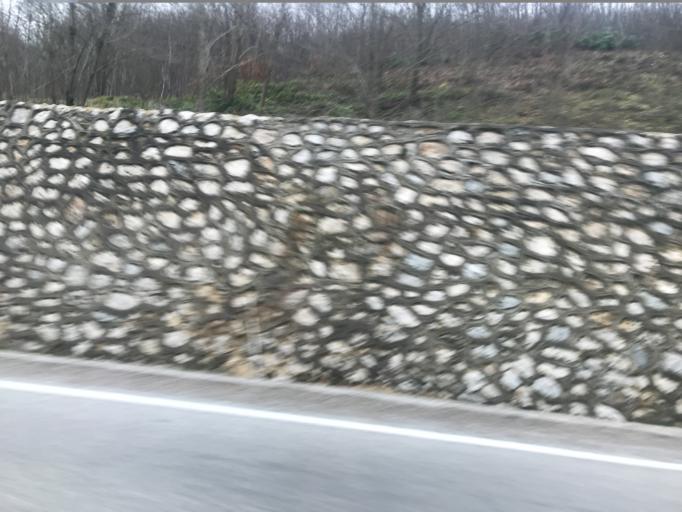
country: TR
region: Bartin
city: Amasra
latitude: 41.7024
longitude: 32.3843
